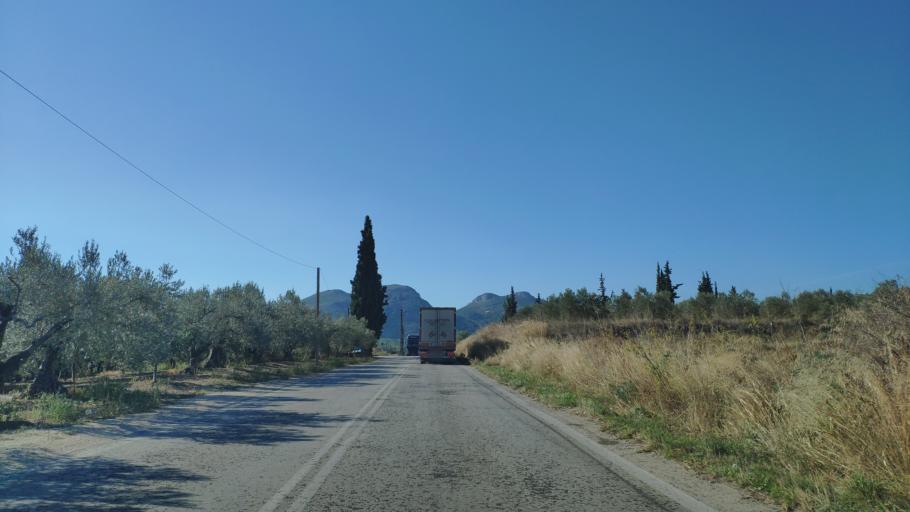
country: GR
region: Peloponnese
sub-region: Nomos Korinthias
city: Arkhaia Korinthos
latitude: 37.8858
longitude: 22.8943
